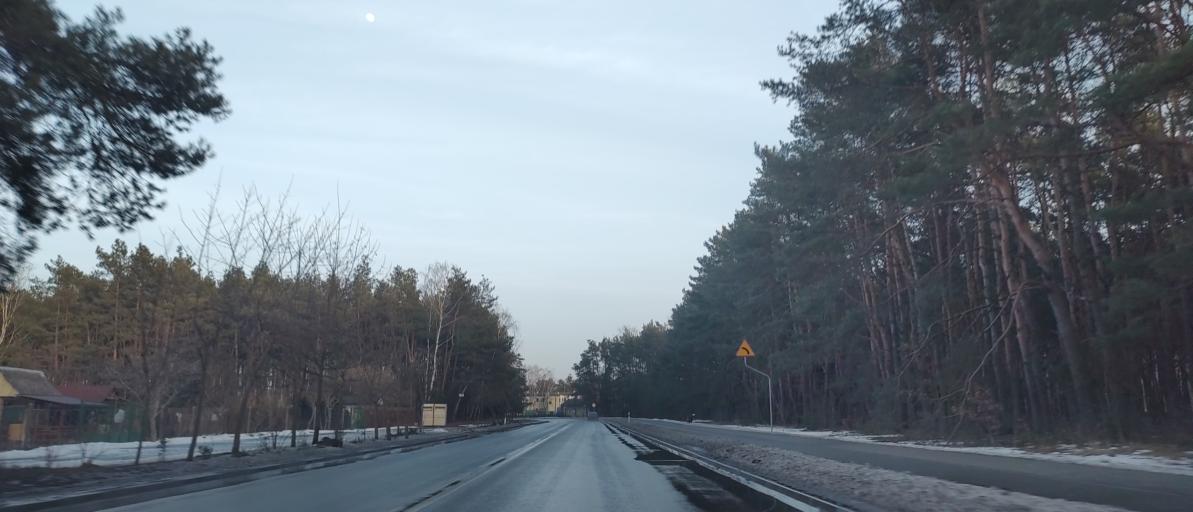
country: PL
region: Masovian Voivodeship
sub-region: Powiat bialobrzeski
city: Bialobrzegi
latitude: 51.6429
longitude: 20.9393
